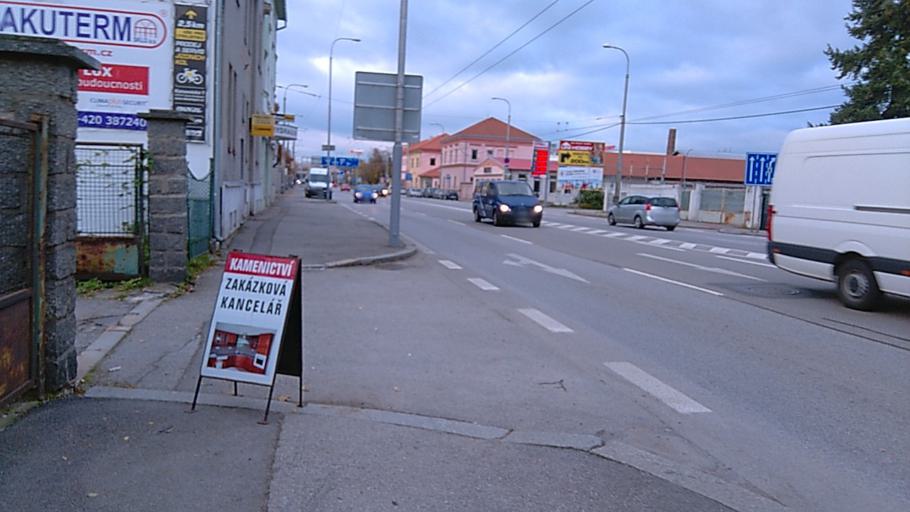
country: CZ
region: Jihocesky
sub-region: Okres Ceske Budejovice
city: Ceske Budejovice
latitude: 48.9925
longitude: 14.4768
